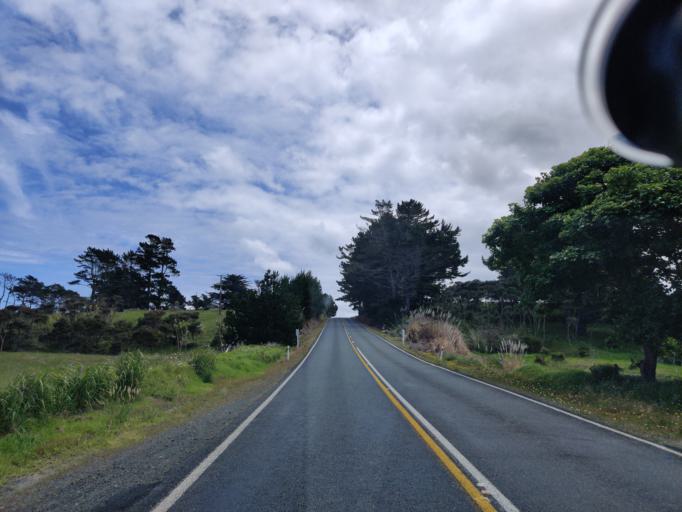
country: NZ
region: Northland
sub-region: Far North District
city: Kaitaia
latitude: -34.6787
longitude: 173.0046
